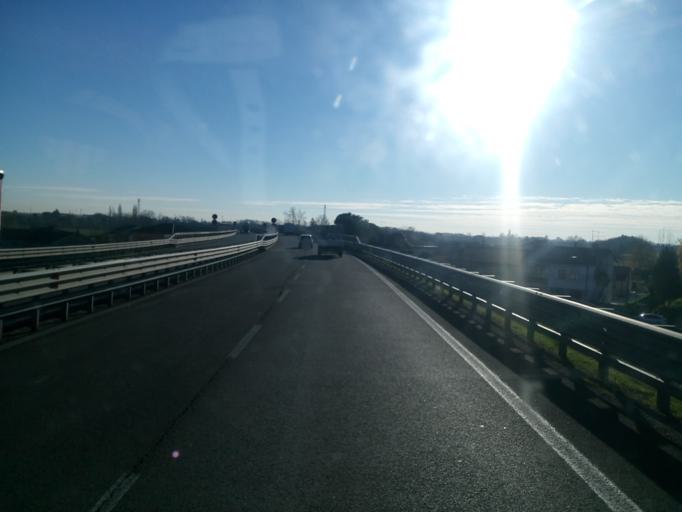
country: IT
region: Veneto
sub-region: Provincia di Treviso
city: Sant'Andrea
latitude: 45.6674
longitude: 11.9058
